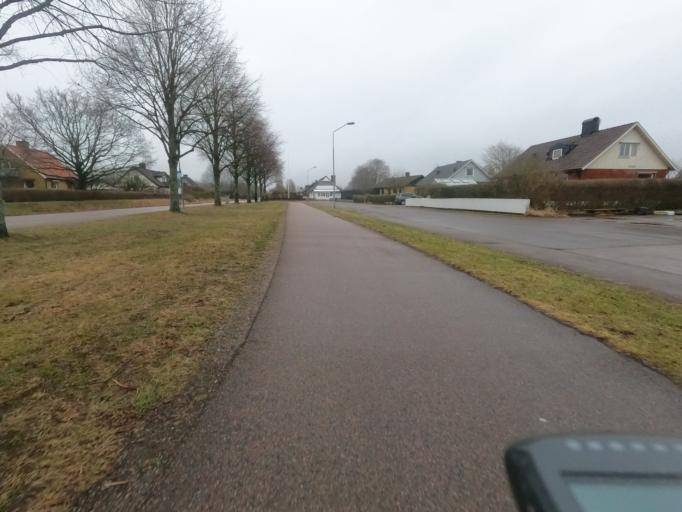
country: SE
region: Halland
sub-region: Halmstads Kommun
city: Fyllinge
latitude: 56.6791
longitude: 12.9310
